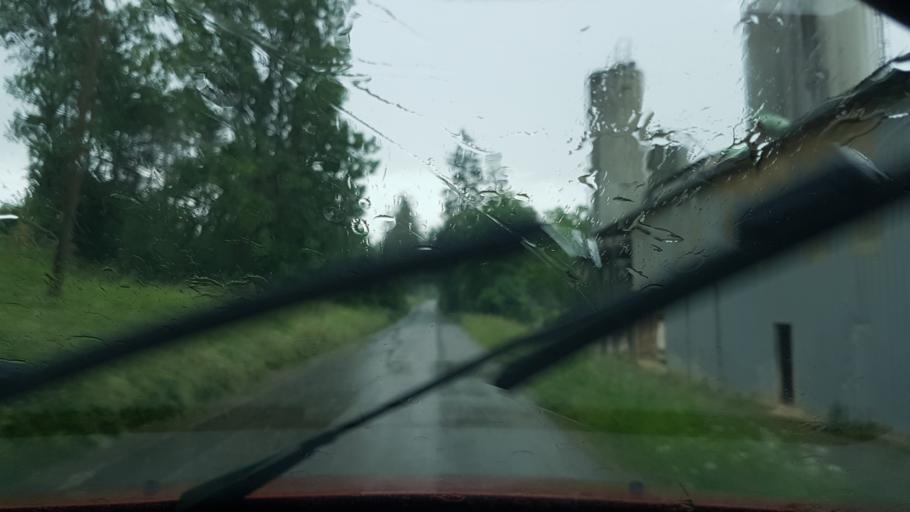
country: FR
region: Franche-Comte
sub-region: Departement du Jura
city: Clairvaux-les-Lacs
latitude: 46.5834
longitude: 5.7023
